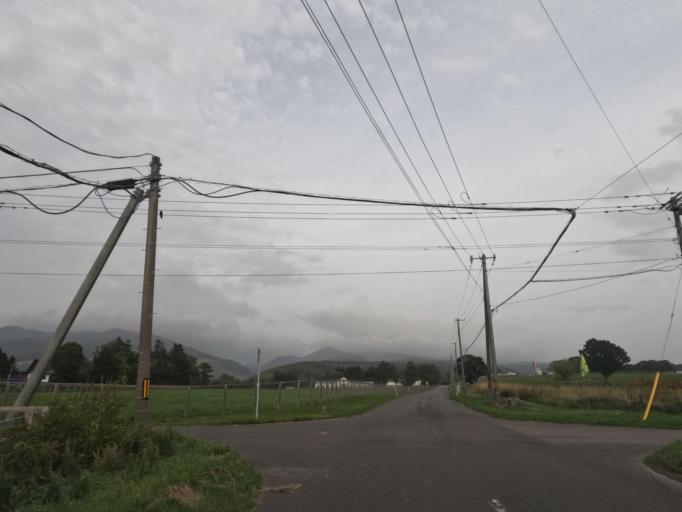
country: JP
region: Hokkaido
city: Date
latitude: 42.4270
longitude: 140.9151
